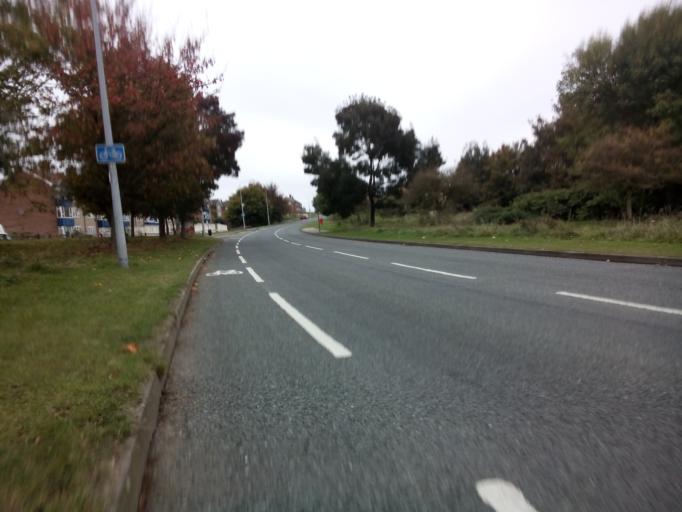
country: GB
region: England
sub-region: Suffolk
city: Ipswich
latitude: 52.0406
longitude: 1.1246
